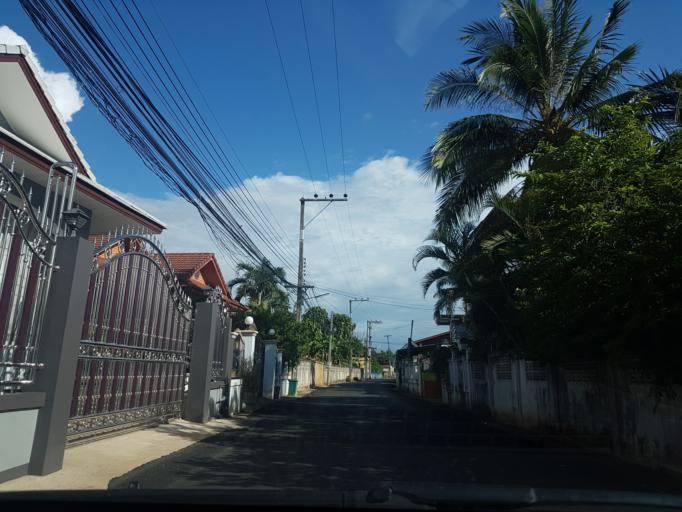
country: TH
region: Lampang
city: Ko Kha
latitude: 18.2289
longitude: 99.4205
